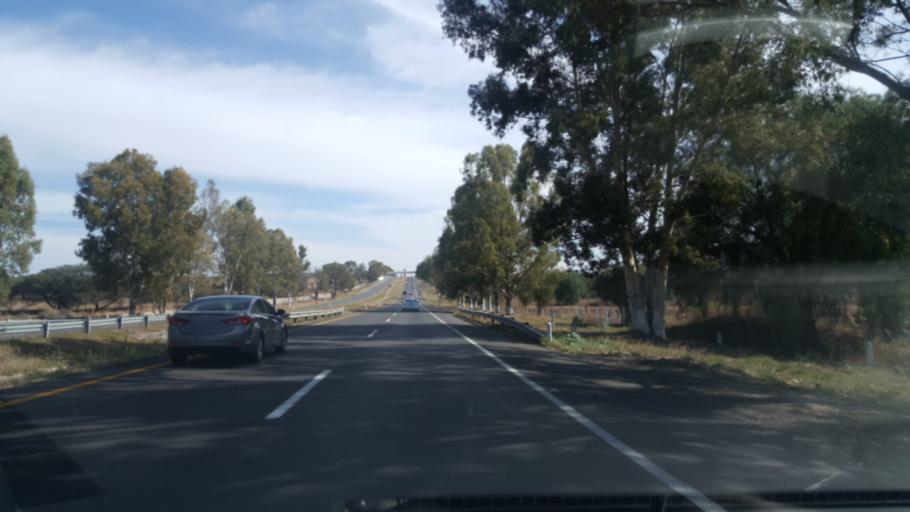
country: MX
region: Jalisco
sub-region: Lagos de Moreno
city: Cristeros [Fraccionamiento]
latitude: 21.2804
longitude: -101.9927
